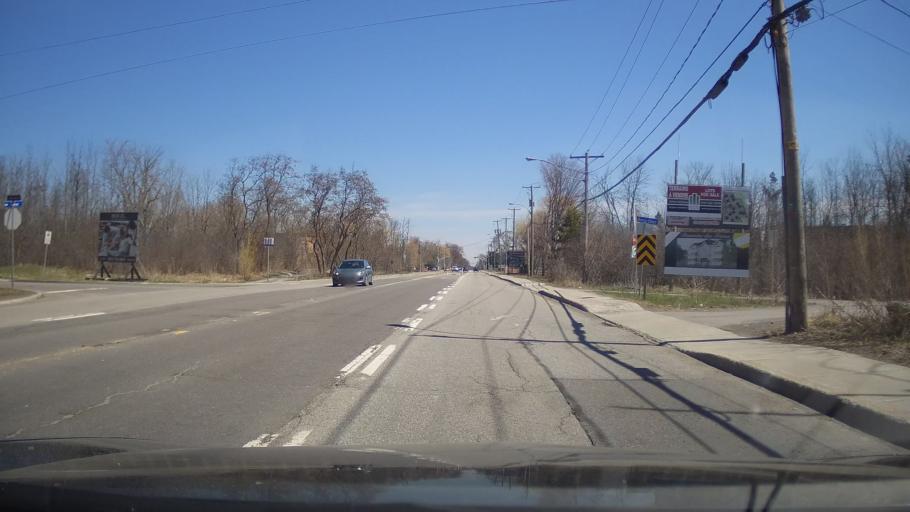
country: CA
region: Ontario
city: Bells Corners
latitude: 45.4017
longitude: -75.8067
